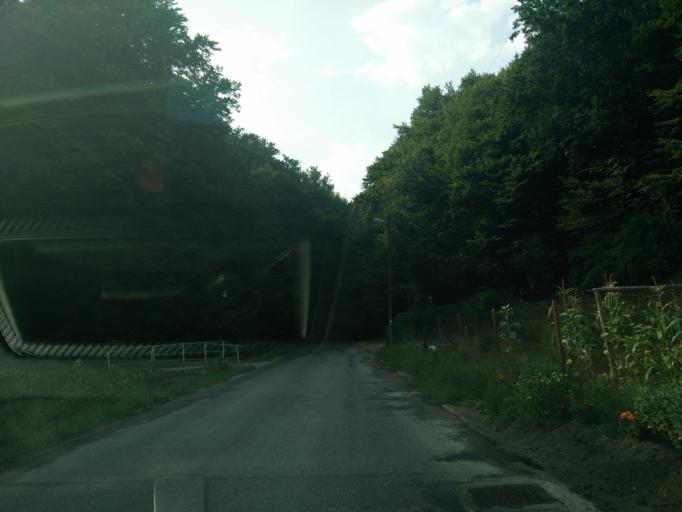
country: SK
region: Banskobystricky
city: Zarnovica
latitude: 48.5104
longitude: 18.7786
